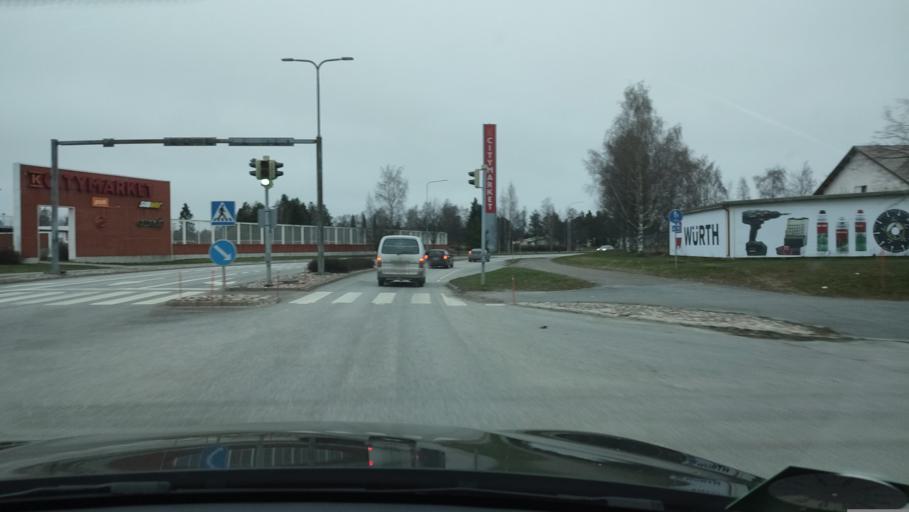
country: FI
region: Southern Ostrobothnia
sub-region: Suupohja
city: Kauhajoki
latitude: 62.4329
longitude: 22.1803
